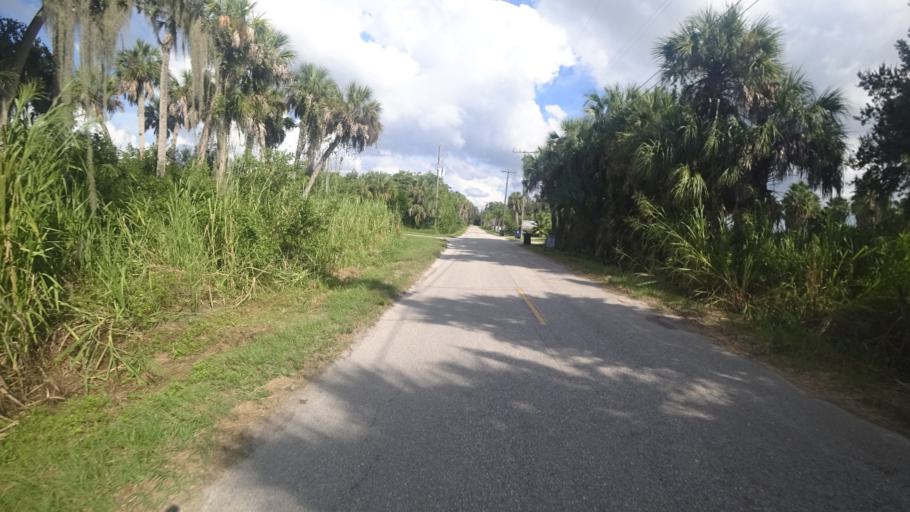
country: US
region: Florida
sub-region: Manatee County
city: Memphis
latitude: 27.5795
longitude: -82.5731
